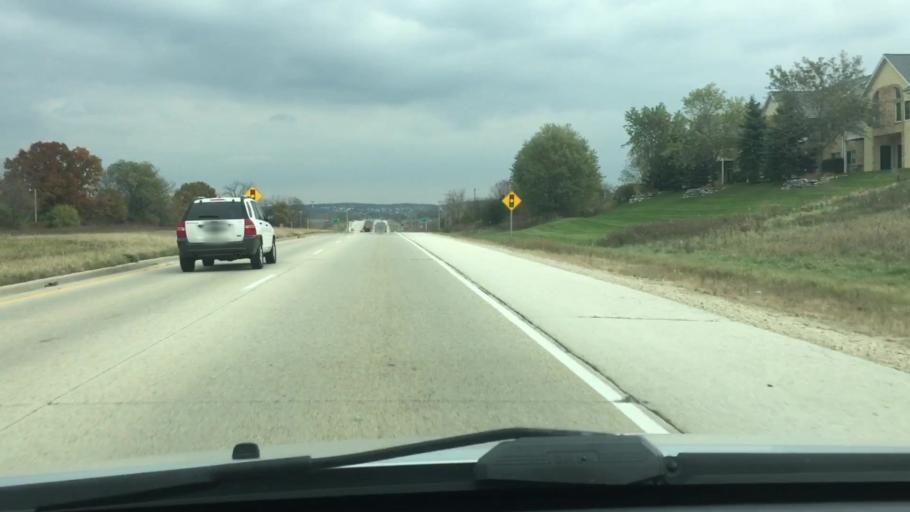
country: US
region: Wisconsin
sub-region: Waukesha County
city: Waukesha
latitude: 42.9767
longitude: -88.2517
